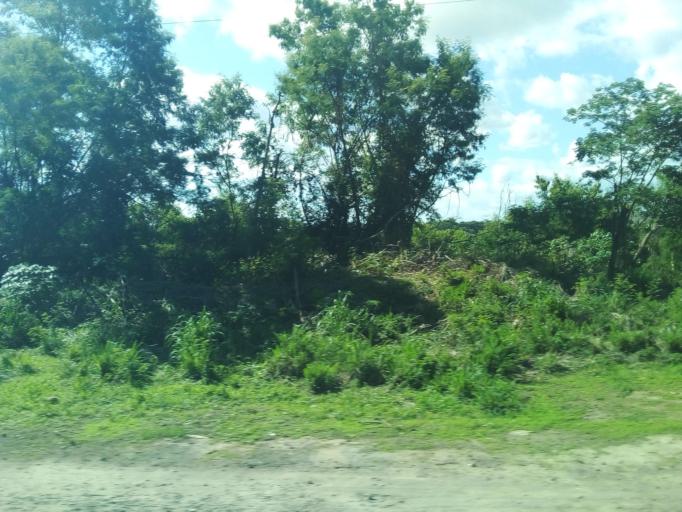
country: BR
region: Minas Gerais
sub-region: Governador Valadares
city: Governador Valadares
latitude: -18.8740
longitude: -41.7824
